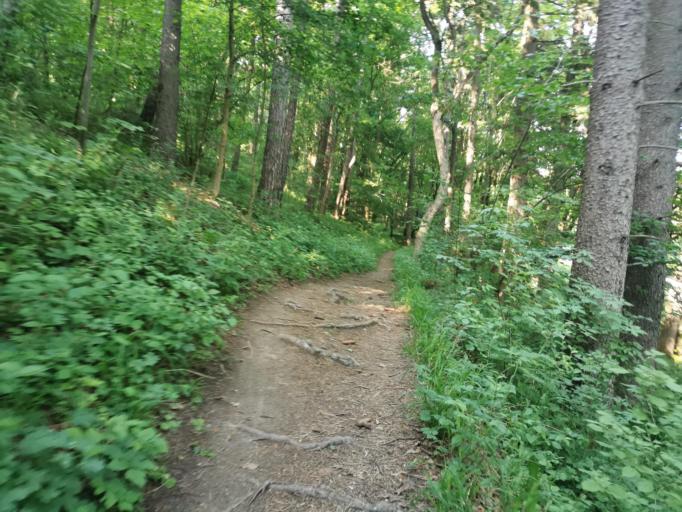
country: CZ
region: South Moravian
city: Knezdub
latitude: 48.8576
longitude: 17.3756
